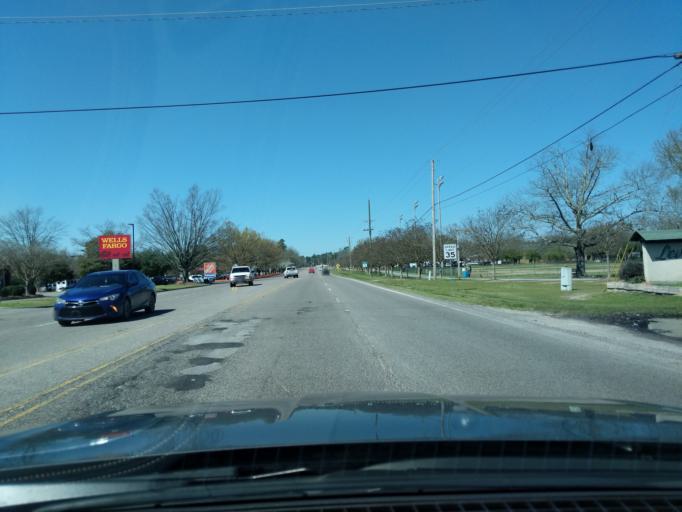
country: US
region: South Carolina
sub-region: Aiken County
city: Aiken
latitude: 33.5243
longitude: -81.7200
